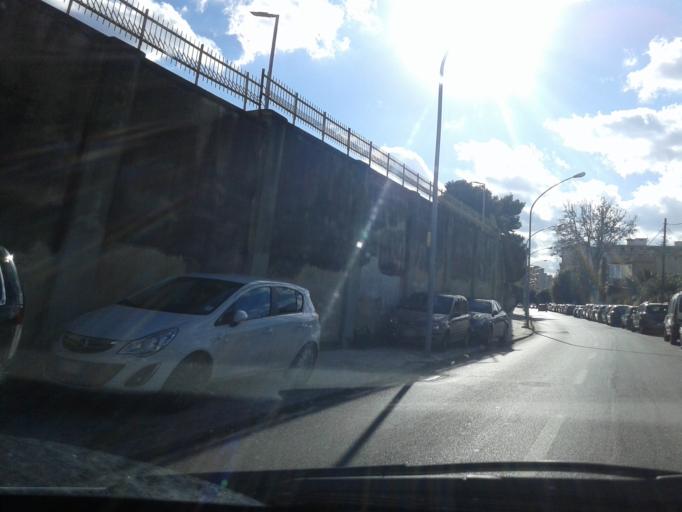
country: IT
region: Sicily
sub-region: Palermo
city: Palermo
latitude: 38.1042
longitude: 13.3389
